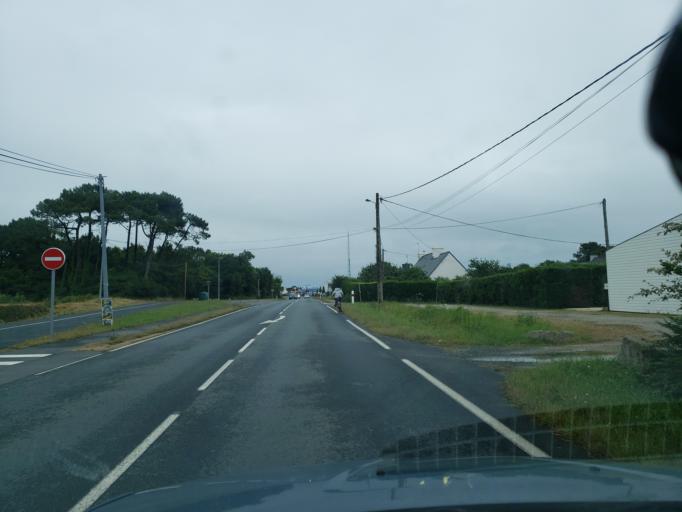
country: FR
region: Brittany
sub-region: Departement du Finistere
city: Plomeur
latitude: 47.8186
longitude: -4.2958
